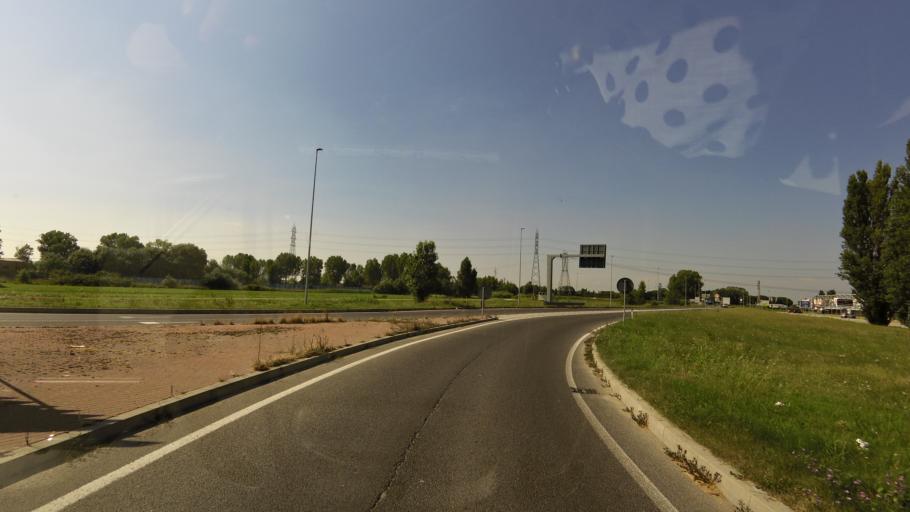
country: IT
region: Emilia-Romagna
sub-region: Provincia di Ravenna
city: Ravenna
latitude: 44.4507
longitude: 12.2097
